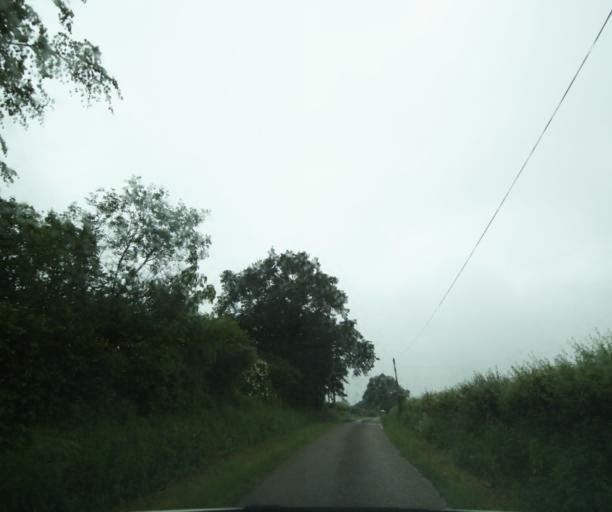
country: FR
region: Bourgogne
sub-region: Departement de Saone-et-Loire
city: Charolles
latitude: 46.4650
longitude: 4.2257
